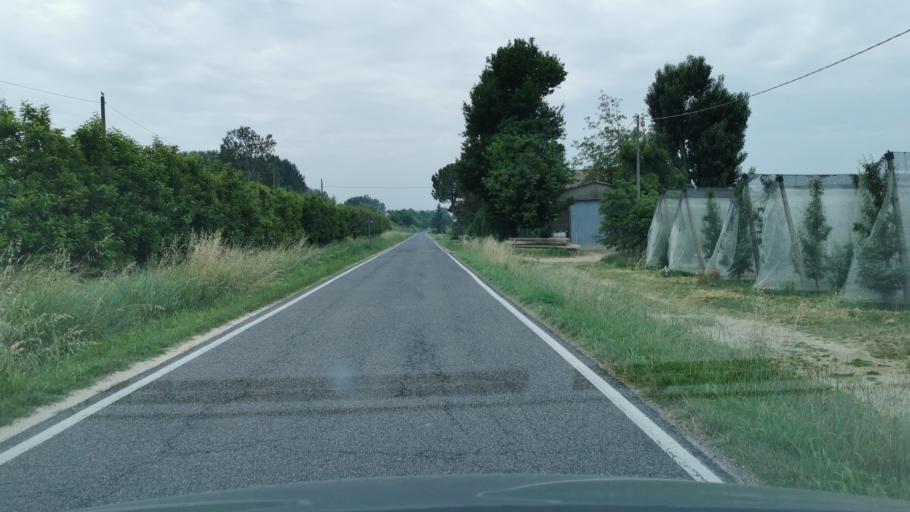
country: IT
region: Emilia-Romagna
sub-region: Provincia di Ravenna
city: Russi
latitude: 44.3963
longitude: 12.0166
